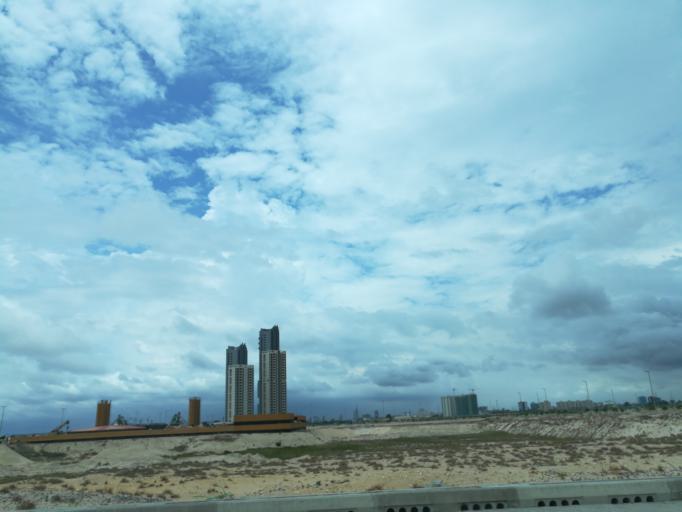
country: NG
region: Lagos
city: Ikoyi
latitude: 6.4034
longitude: 3.4136
